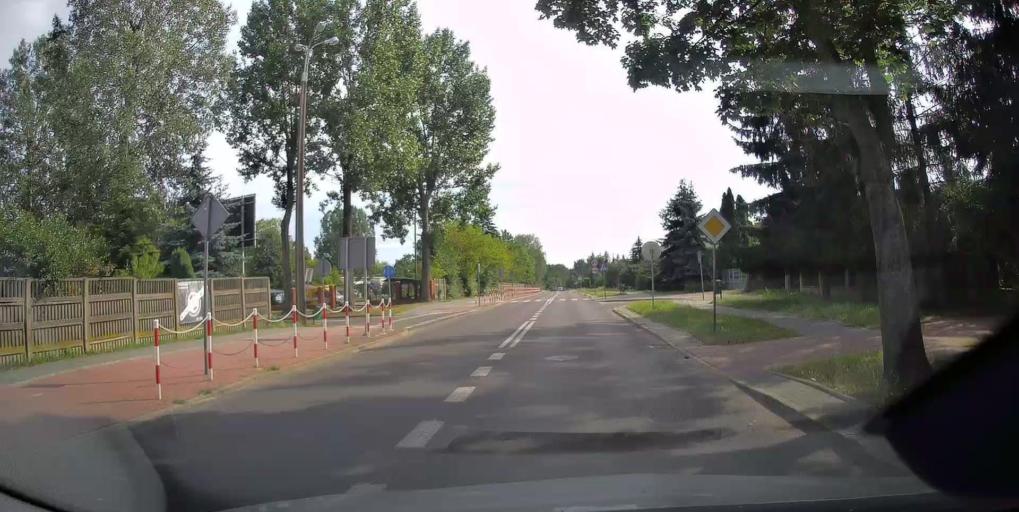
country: PL
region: Lodz Voivodeship
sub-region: Powiat tomaszowski
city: Tomaszow Mazowiecki
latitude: 51.5195
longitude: 20.0026
